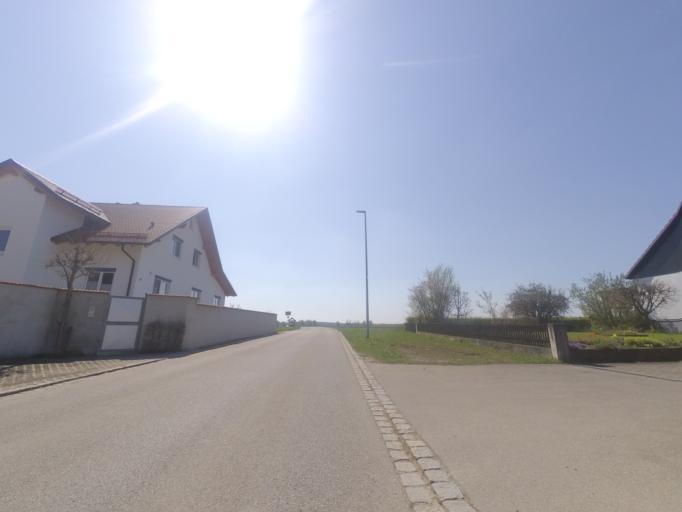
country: DE
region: Bavaria
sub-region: Swabia
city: Pfaffenhofen an der Roth
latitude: 48.3410
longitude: 10.1989
